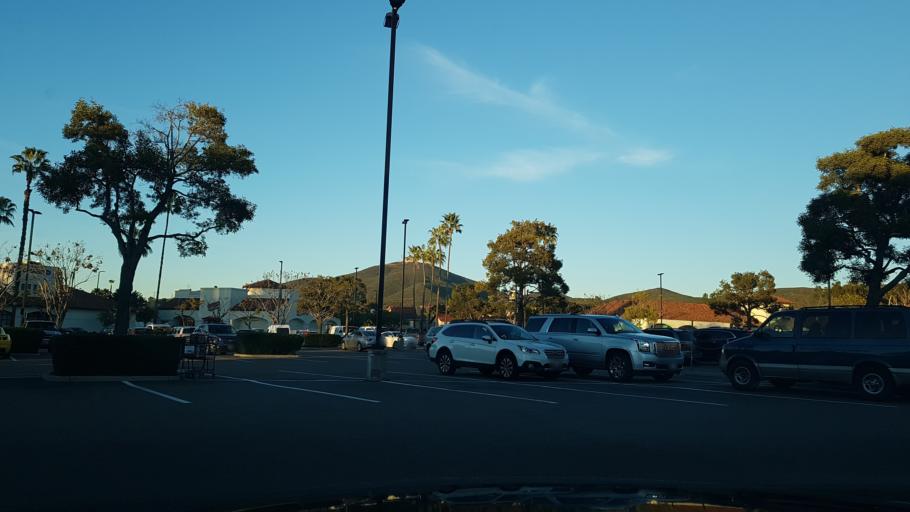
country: US
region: California
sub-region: San Diego County
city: Fairbanks Ranch
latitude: 32.9579
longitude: -117.1259
